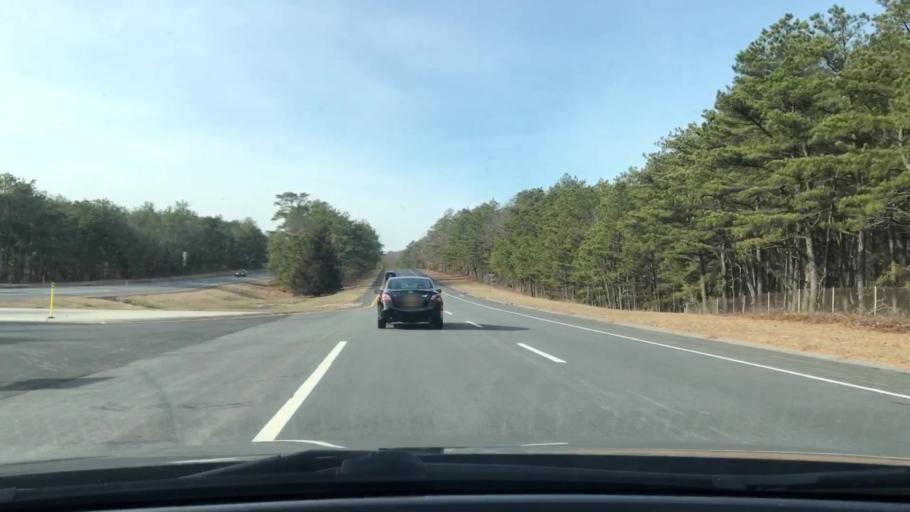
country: US
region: New York
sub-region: Suffolk County
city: Calverton
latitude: 40.9068
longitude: -72.7087
